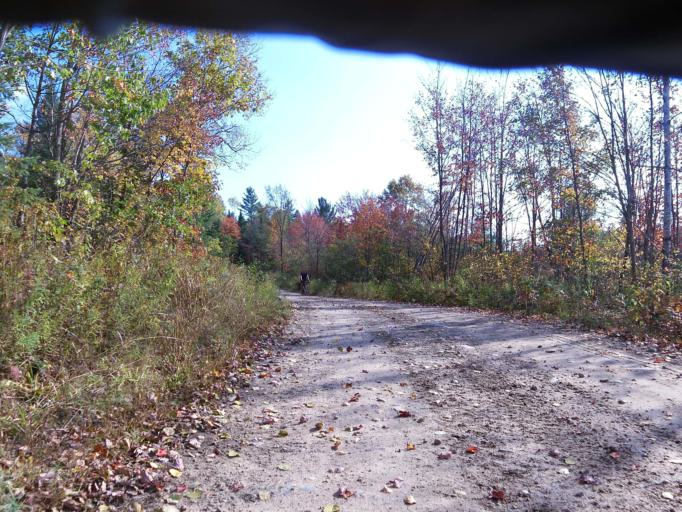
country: CA
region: Ontario
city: Petawawa
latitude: 45.7992
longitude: -77.3165
